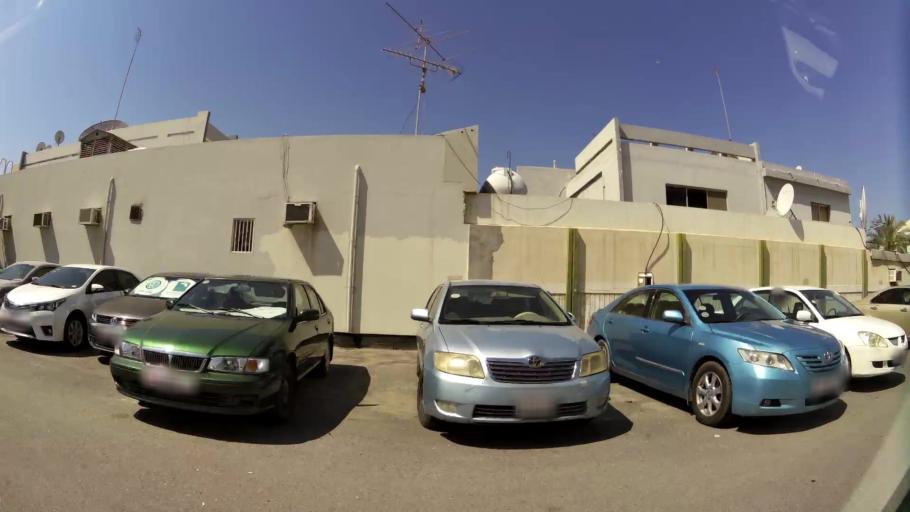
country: BH
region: Manama
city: Manama
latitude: 26.2072
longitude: 50.5976
